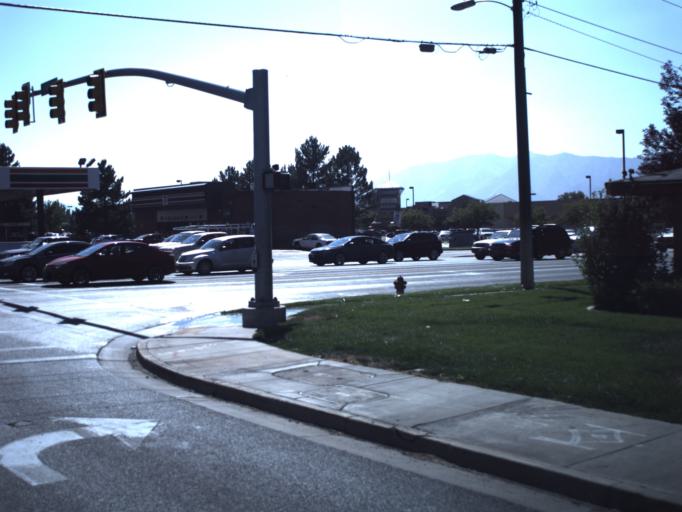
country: US
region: Utah
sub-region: Cache County
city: Logan
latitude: 41.7579
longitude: -111.8345
